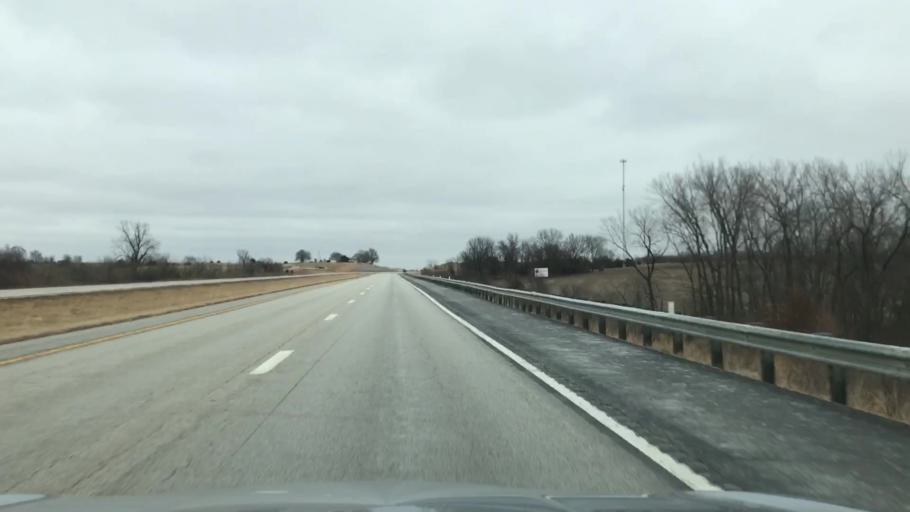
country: US
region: Missouri
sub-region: Caldwell County
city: Hamilton
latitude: 39.7490
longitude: -94.0620
